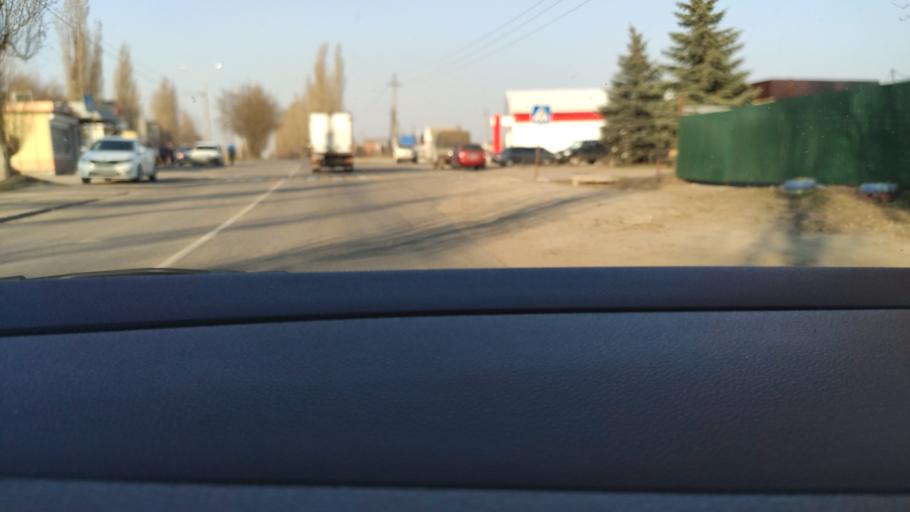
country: RU
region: Voronezj
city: Maslovka
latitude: 51.5841
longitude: 39.3191
